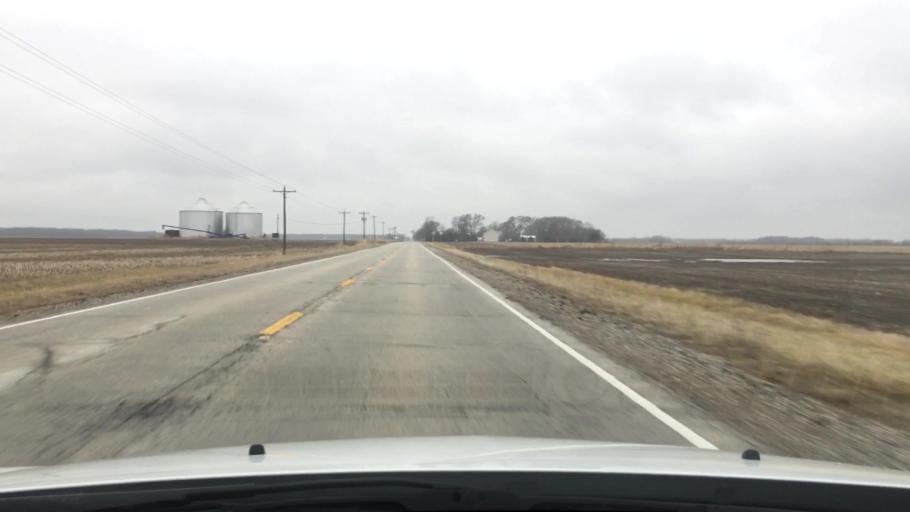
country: US
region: Illinois
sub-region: Iroquois County
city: Watseka
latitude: 40.8888
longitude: -87.7868
